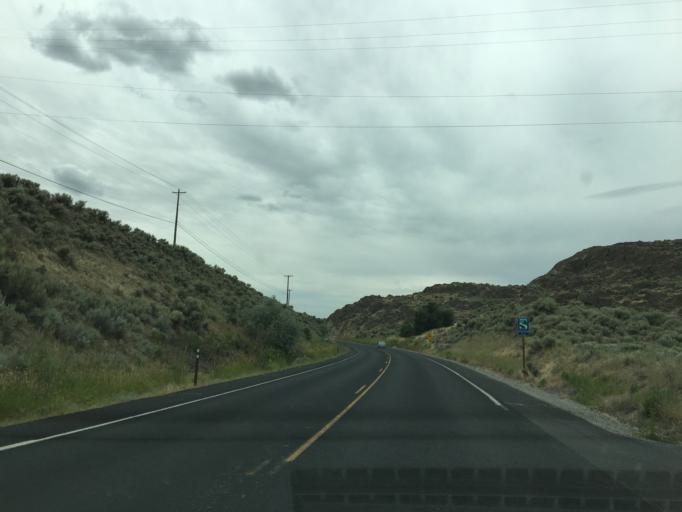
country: US
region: Washington
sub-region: Okanogan County
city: Coulee Dam
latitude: 47.9289
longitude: -119.0444
